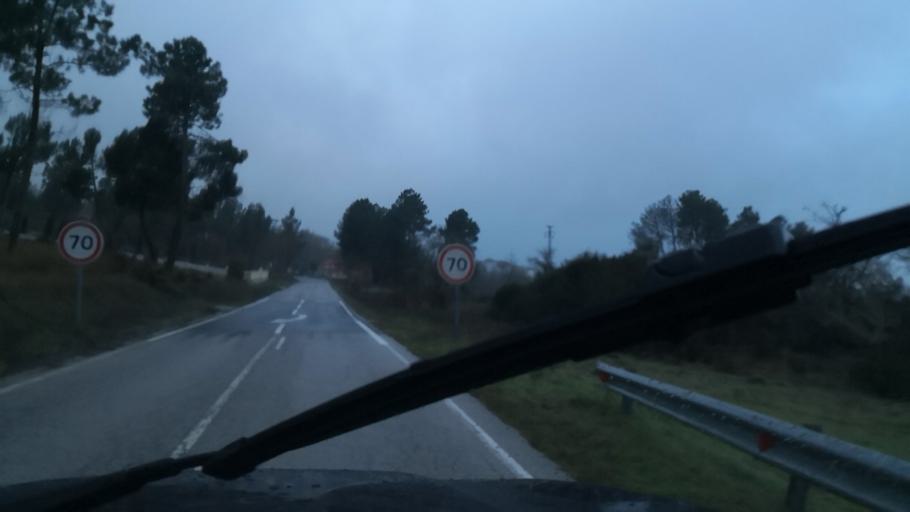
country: PT
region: Vila Real
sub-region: Murca
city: Murca
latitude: 41.4371
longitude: -7.5450
